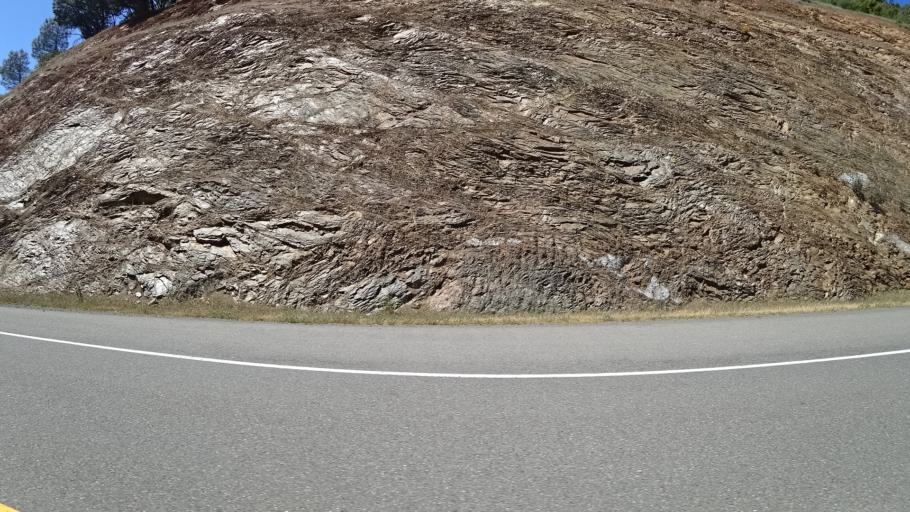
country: US
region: California
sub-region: Trinity County
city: Weaverville
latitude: 40.7358
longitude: -123.0142
